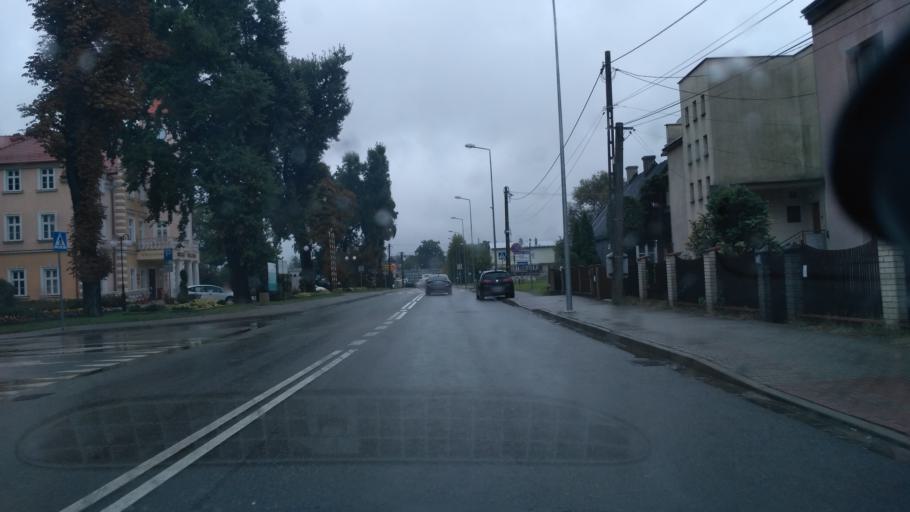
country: PL
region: Subcarpathian Voivodeship
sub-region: Powiat debicki
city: Debica
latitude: 50.0588
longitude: 21.4075
